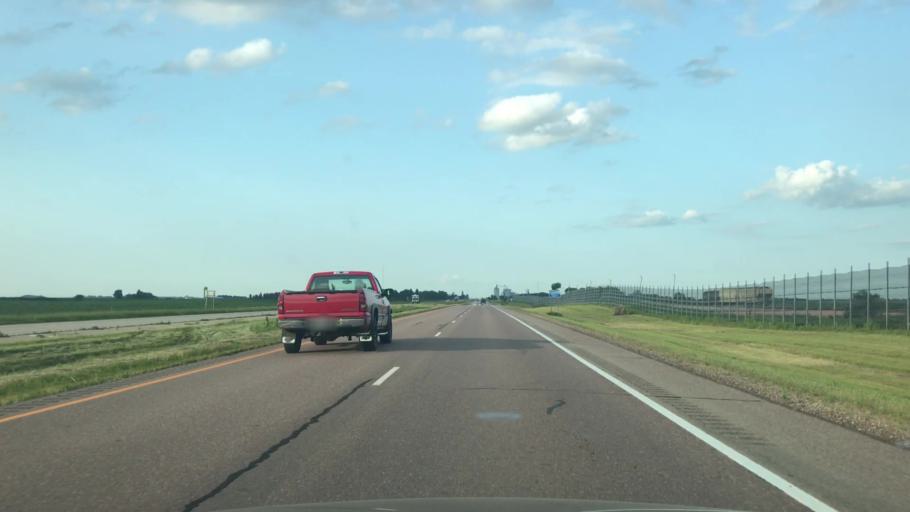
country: US
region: Minnesota
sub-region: Nobles County
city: Worthington
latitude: 43.6759
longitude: -95.5065
